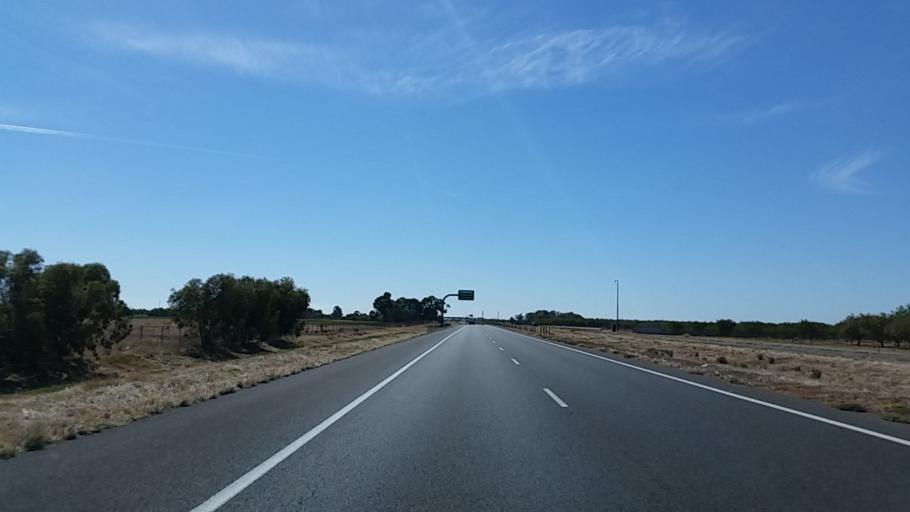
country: AU
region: South Australia
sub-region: Playford
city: Angle Vale
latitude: -34.6473
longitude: 138.6647
